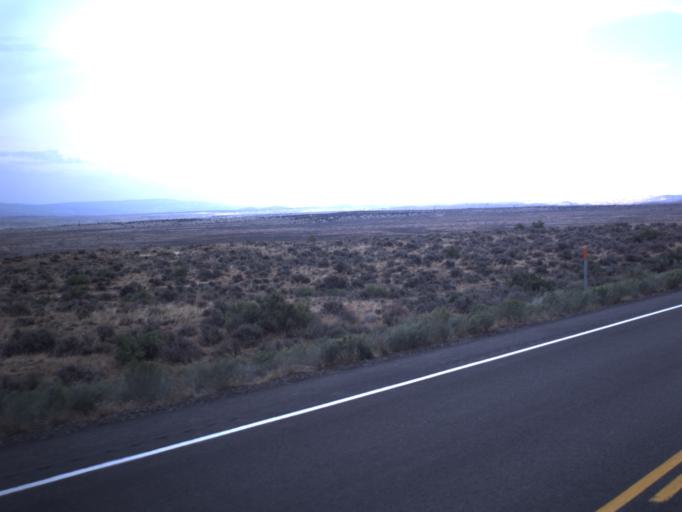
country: US
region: Utah
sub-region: Uintah County
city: Naples
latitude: 40.2536
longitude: -109.4307
